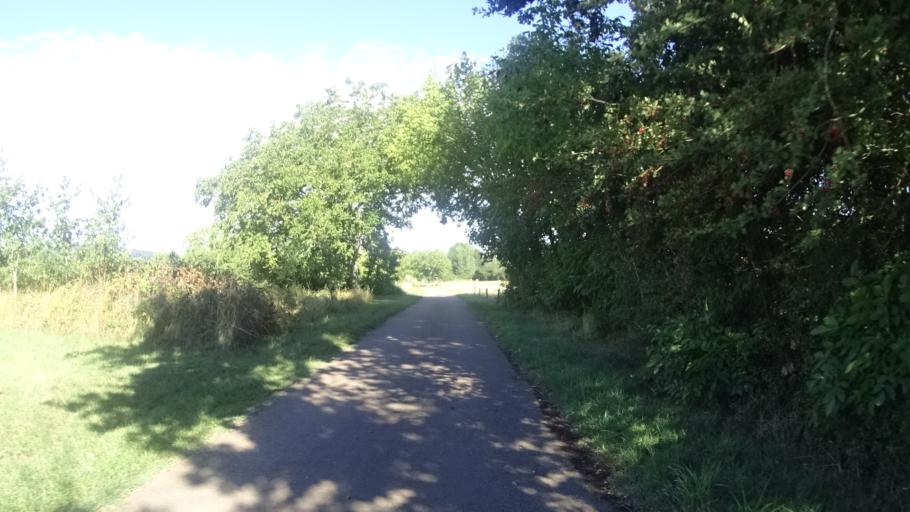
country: FR
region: Centre
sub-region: Departement du Cher
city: Sancerre
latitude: 47.3172
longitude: 2.8725
